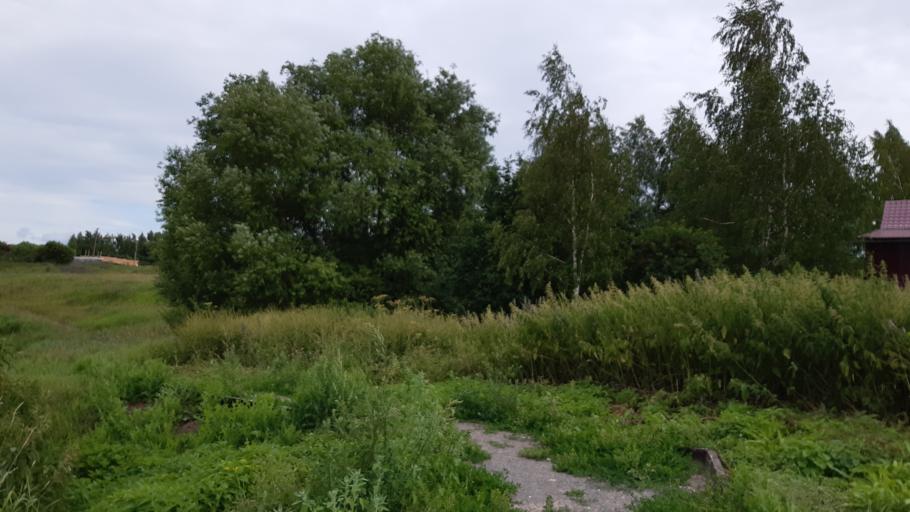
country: RU
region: Tula
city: Yepifan'
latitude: 53.6697
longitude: 38.6520
